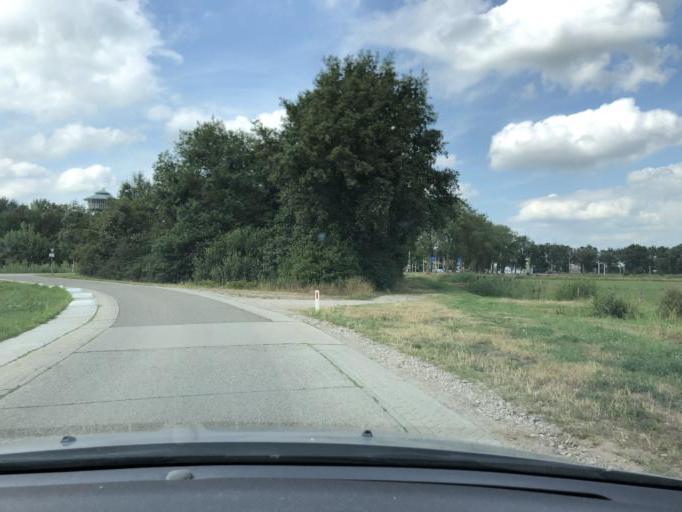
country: NL
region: Overijssel
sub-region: Gemeente Staphorst
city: Staphorst
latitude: 52.5812
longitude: 6.1953
